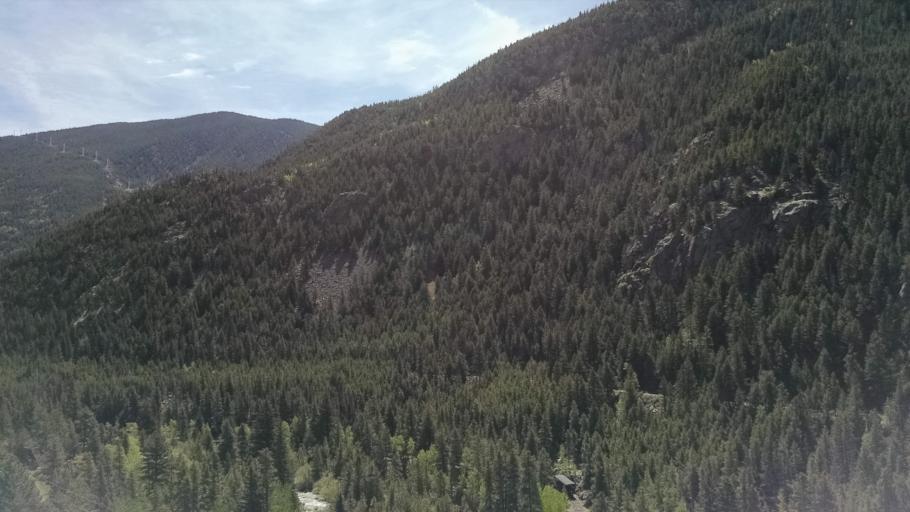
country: US
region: Colorado
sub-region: Clear Creek County
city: Georgetown
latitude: 39.6994
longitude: -105.7108
